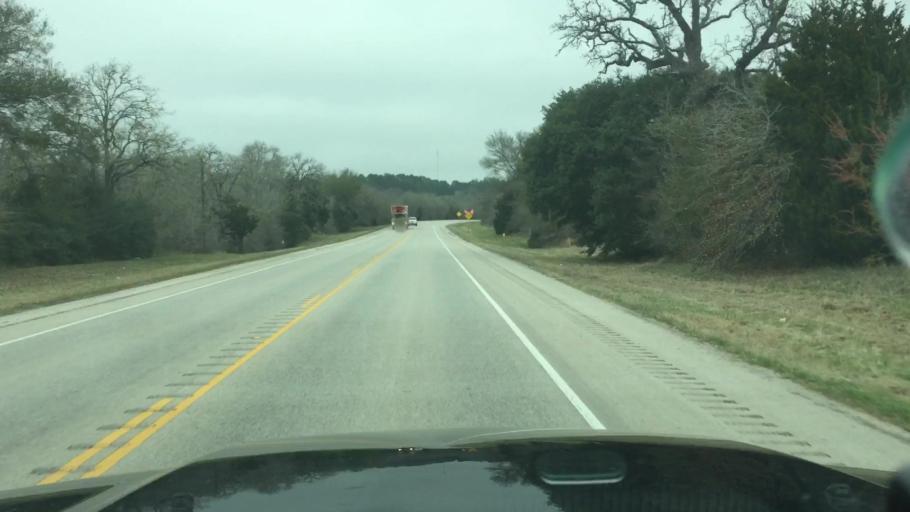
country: US
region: Texas
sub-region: Fayette County
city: La Grange
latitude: 30.0307
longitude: -96.9071
